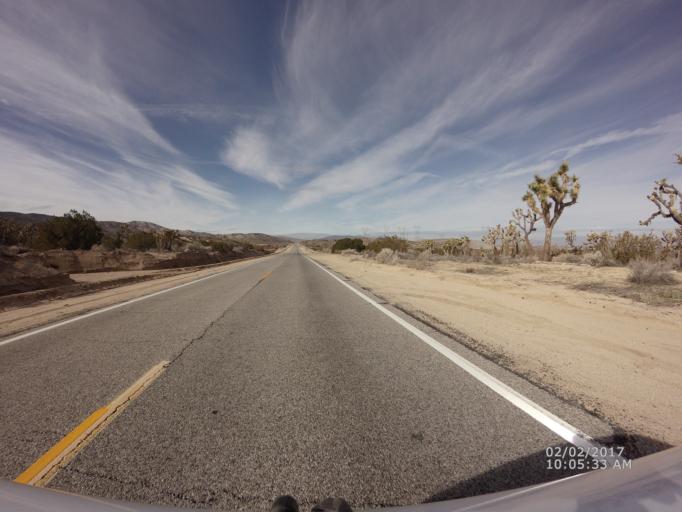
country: US
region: California
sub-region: Los Angeles County
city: Littlerock
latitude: 34.5066
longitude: -117.9894
